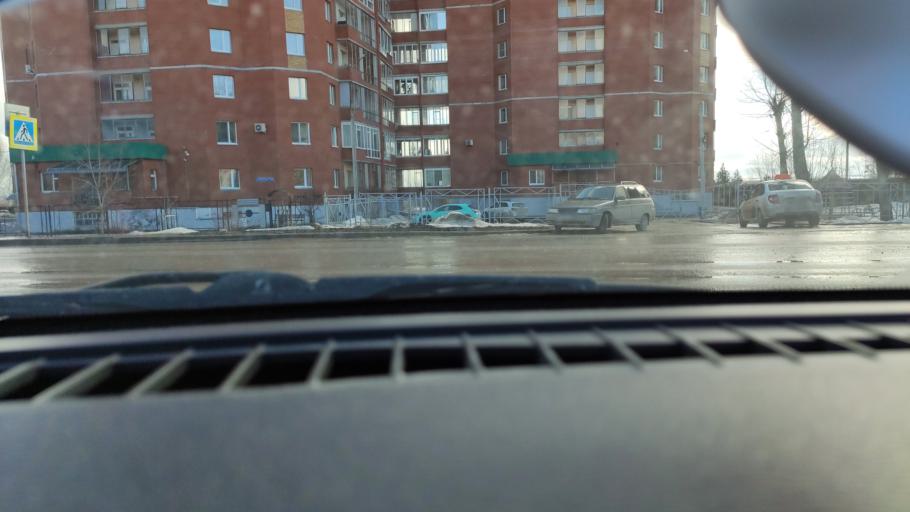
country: RU
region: Perm
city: Kultayevo
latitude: 58.0027
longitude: 55.9647
